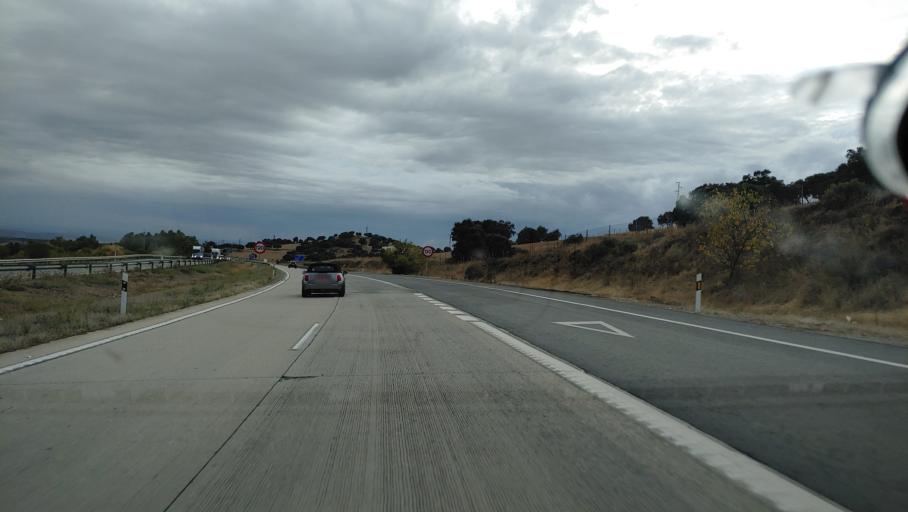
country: ES
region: Andalusia
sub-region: Provincia de Jaen
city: Santa Elena
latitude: 38.3129
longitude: -3.5729
